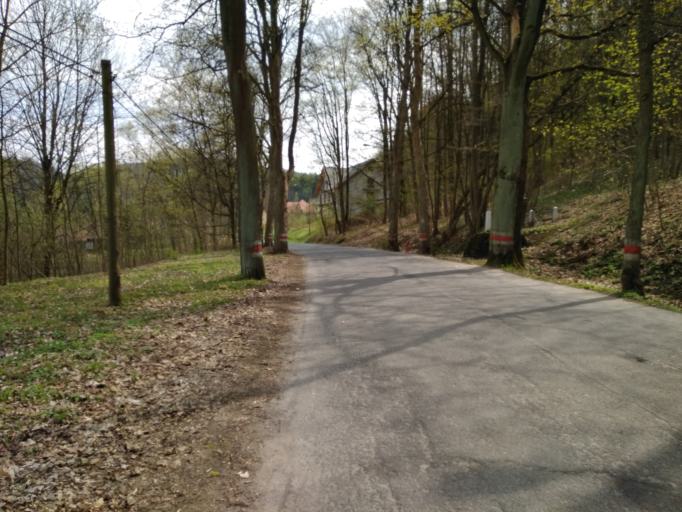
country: PL
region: Lower Silesian Voivodeship
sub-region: Powiat klodzki
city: Kudowa-Zdroj
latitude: 50.4459
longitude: 16.2585
